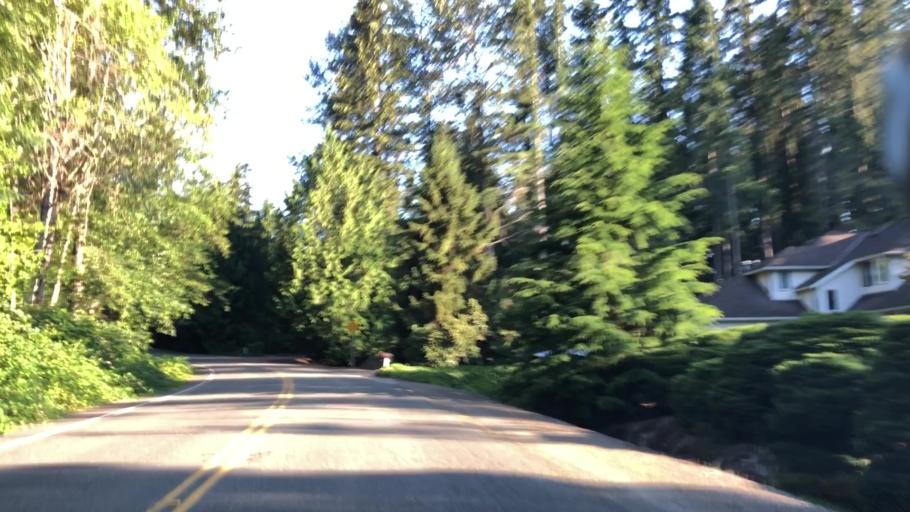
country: US
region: Washington
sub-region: King County
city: Cottage Lake
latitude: 47.7382
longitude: -122.0925
